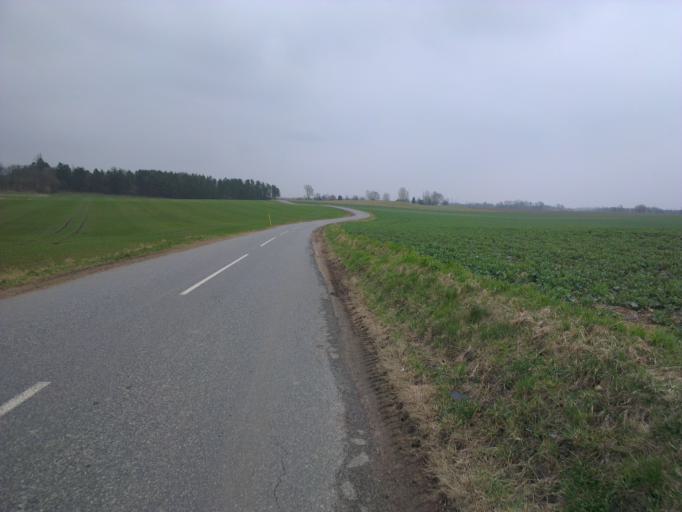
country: DK
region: Capital Region
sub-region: Egedal Kommune
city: Olstykke
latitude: 55.8355
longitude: 12.1230
